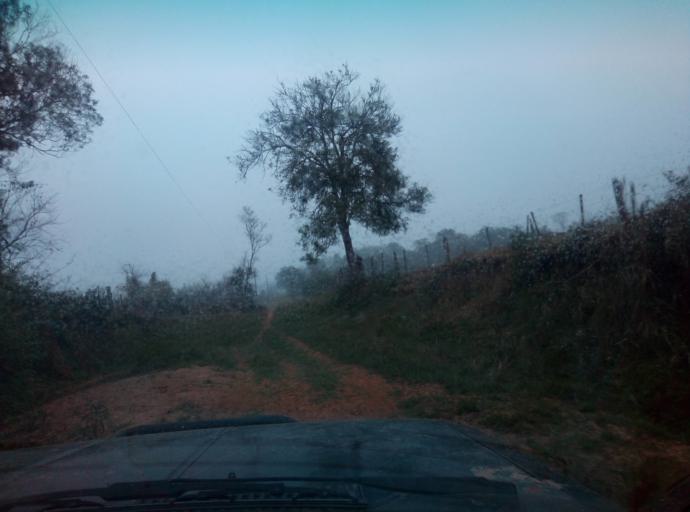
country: PY
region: Caaguazu
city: Doctor Cecilio Baez
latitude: -25.1556
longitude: -56.2612
